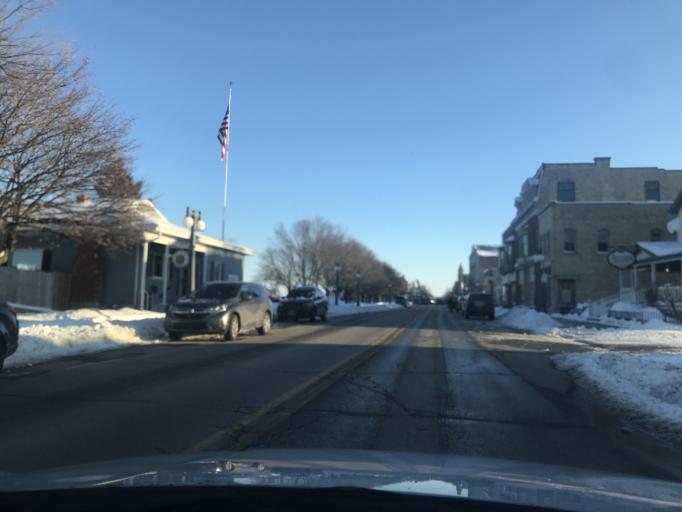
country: US
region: Michigan
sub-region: Menominee County
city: Menominee
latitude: 45.1064
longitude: -87.6045
